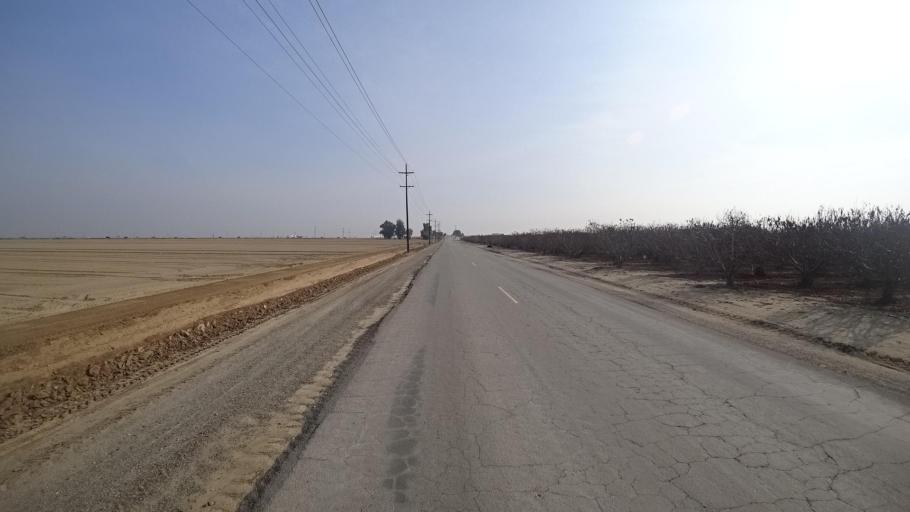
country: US
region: California
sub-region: Kern County
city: Greenfield
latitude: 35.0950
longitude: -119.0457
